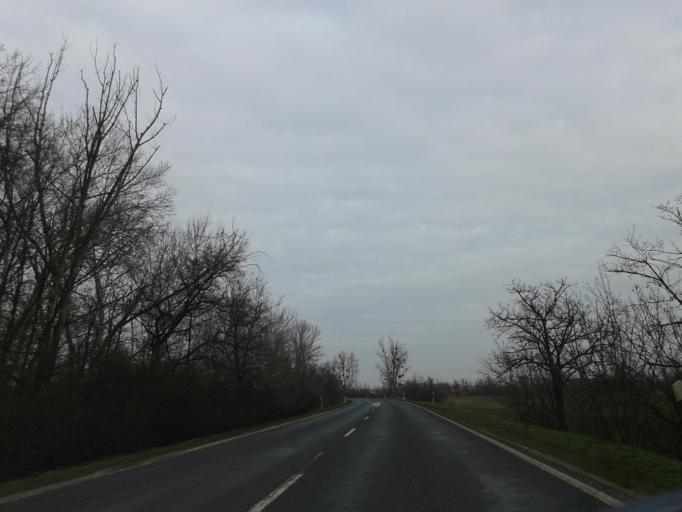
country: HU
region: Komarom-Esztergom
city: Naszaly
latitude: 47.7075
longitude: 18.2932
